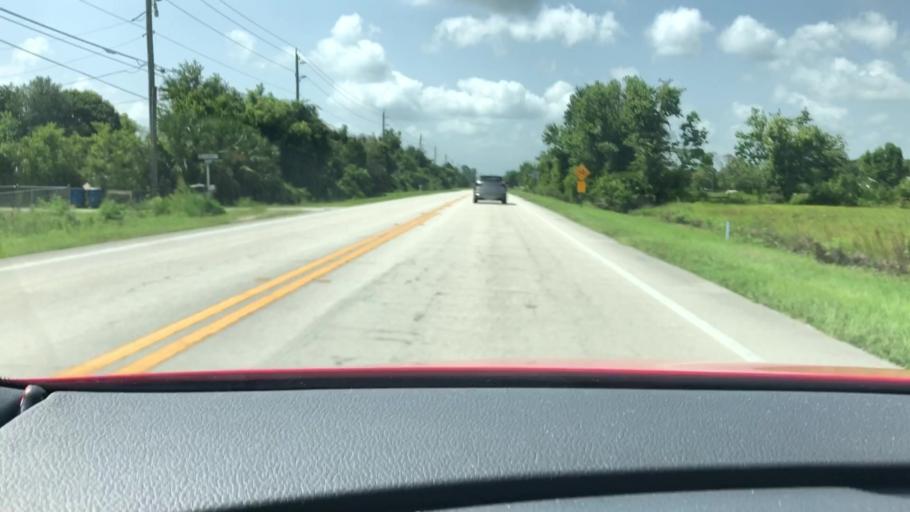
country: US
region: Florida
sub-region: Volusia County
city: Samsula-Spruce Creek
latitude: 29.0814
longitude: -81.0684
